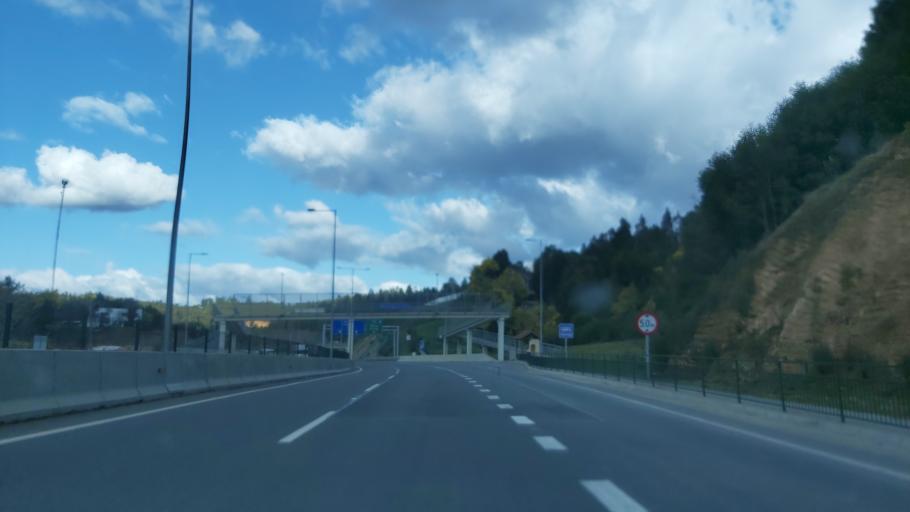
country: CL
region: Biobio
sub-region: Provincia de Concepcion
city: Penco
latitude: -36.8280
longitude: -72.9251
